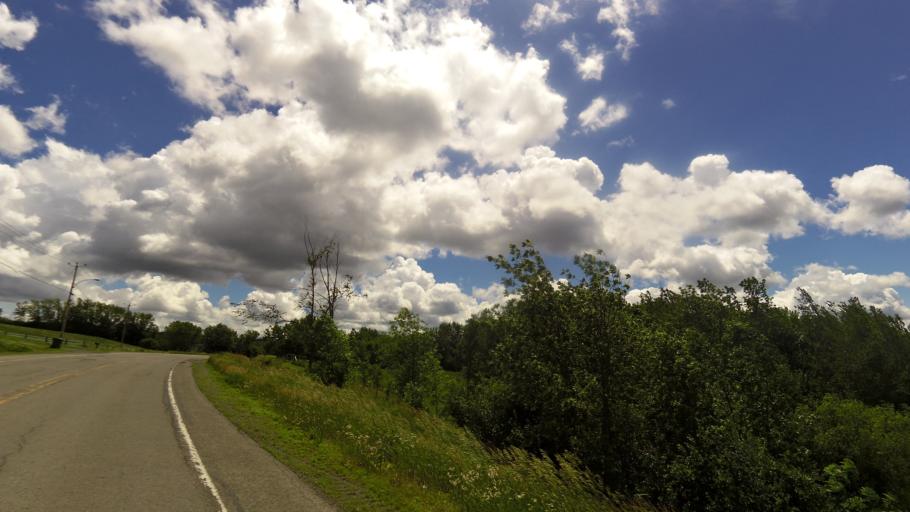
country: CA
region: Quebec
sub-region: Monteregie
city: Rigaud
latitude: 45.5371
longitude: -74.3115
